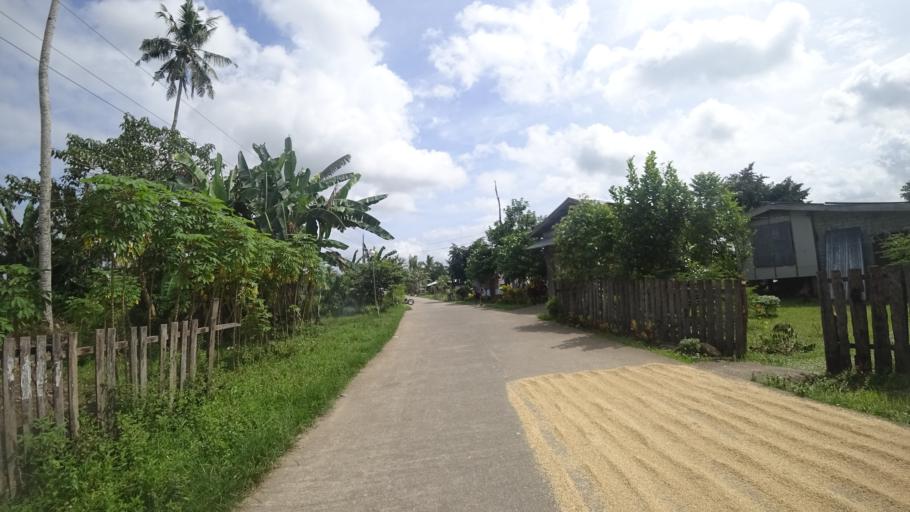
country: PH
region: Eastern Visayas
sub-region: Province of Leyte
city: Santa Fe
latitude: 11.1803
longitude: 124.8895
